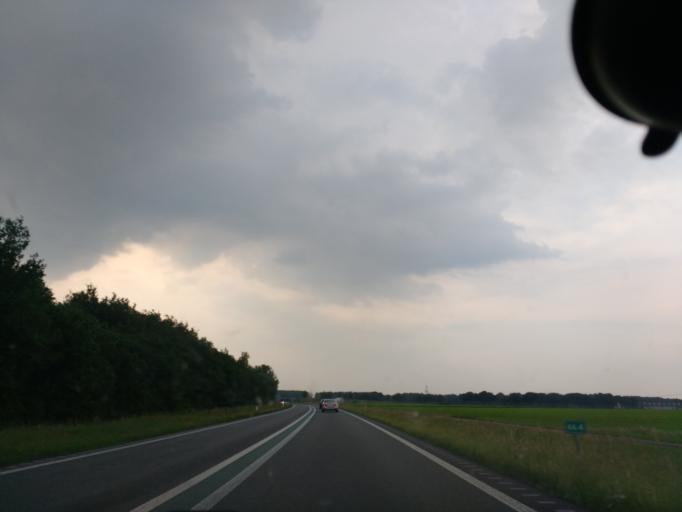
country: NL
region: Drenthe
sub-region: Gemeente Emmen
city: Emmen
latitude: 52.8193
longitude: 6.8542
